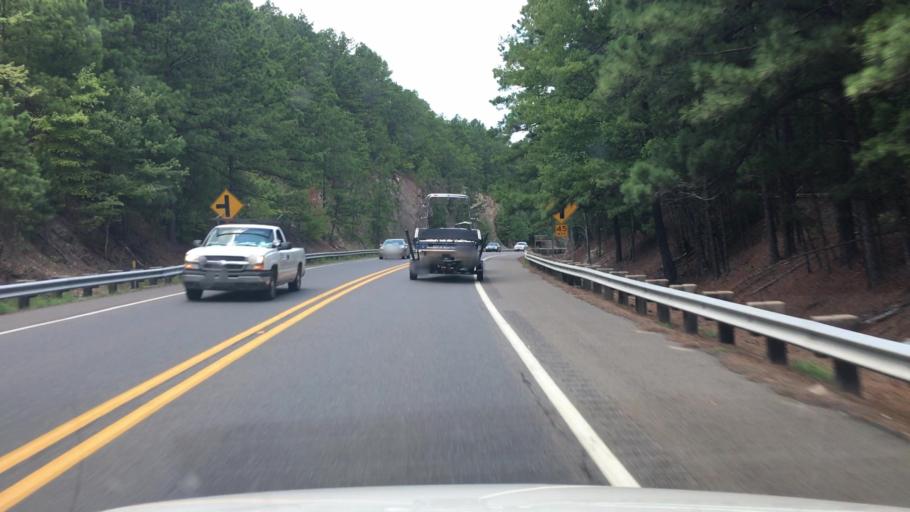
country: US
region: Arkansas
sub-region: Clark County
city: Arkadelphia
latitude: 34.2307
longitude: -93.0969
